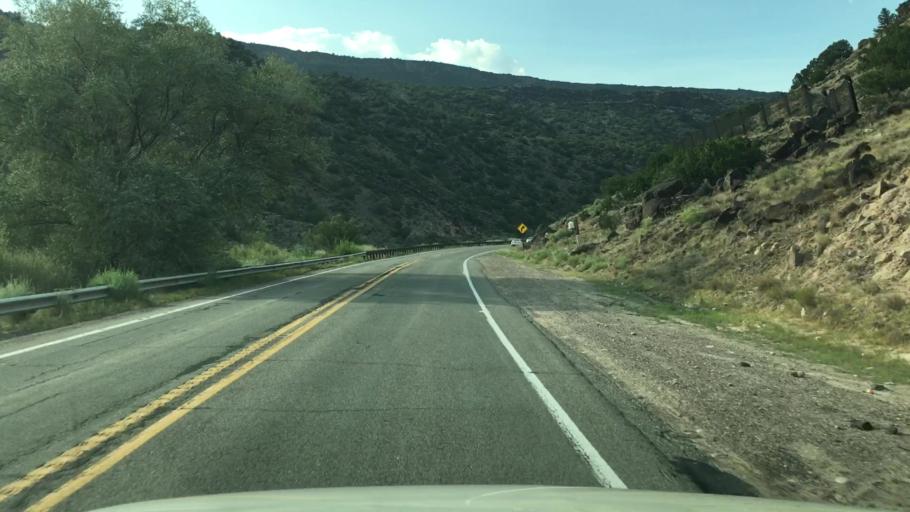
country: US
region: New Mexico
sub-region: Rio Arriba County
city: Ohkay Owingeh
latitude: 36.1836
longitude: -105.9791
